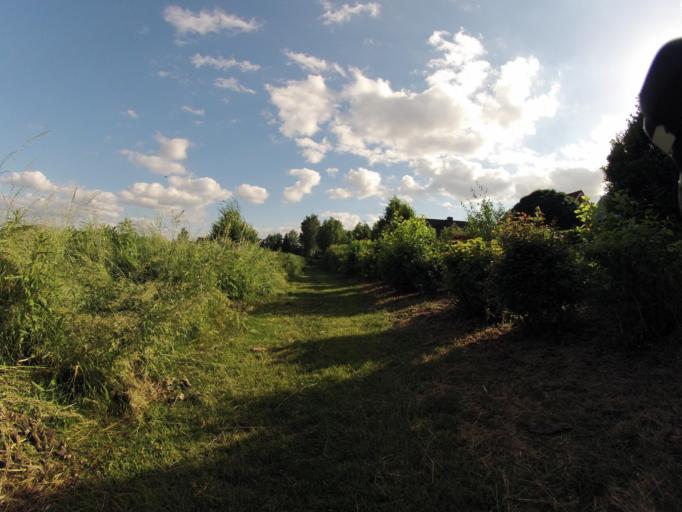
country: DE
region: North Rhine-Westphalia
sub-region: Regierungsbezirk Munster
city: Horstel
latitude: 52.2734
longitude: 7.5947
